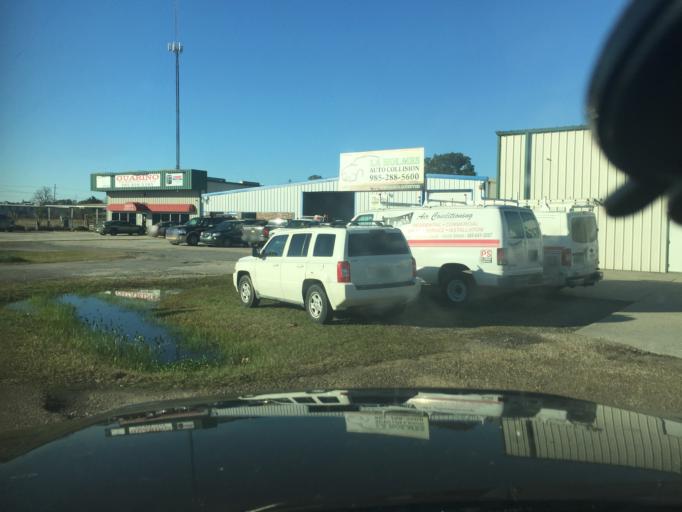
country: US
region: Louisiana
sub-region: Saint Tammany Parish
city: Slidell
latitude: 30.2541
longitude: -89.7617
